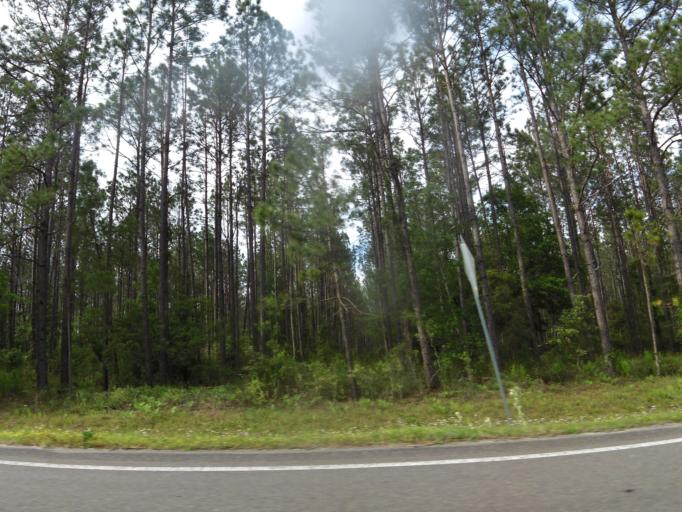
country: US
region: Georgia
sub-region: Camden County
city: Kingsland
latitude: 30.6945
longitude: -81.6931
